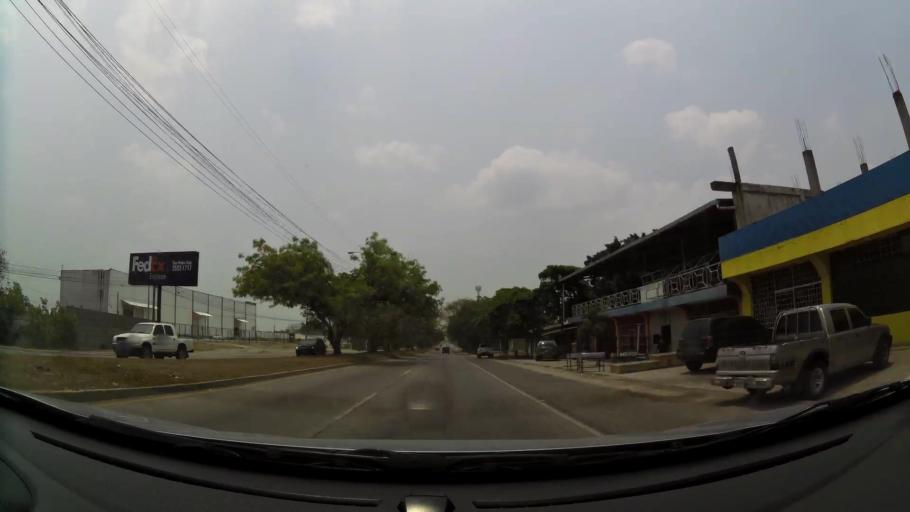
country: HN
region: Cortes
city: La Lima
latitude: 15.4613
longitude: -87.9579
